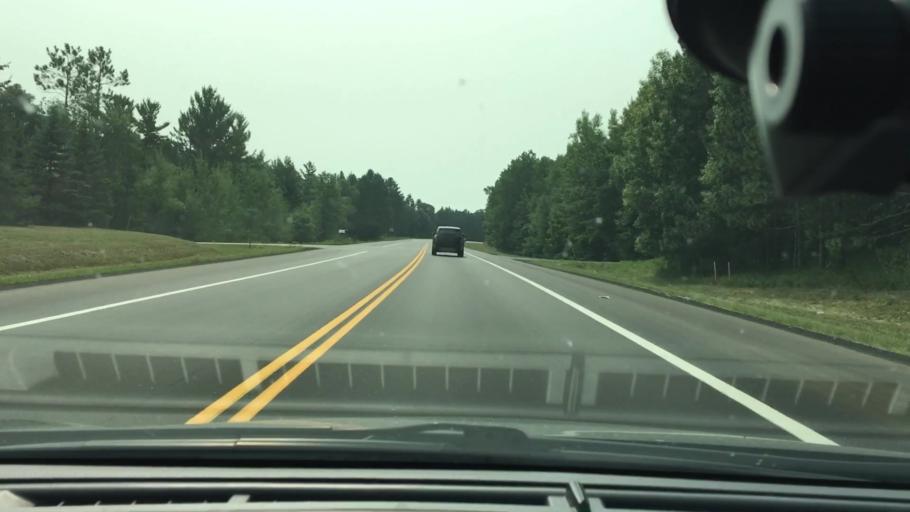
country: US
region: Minnesota
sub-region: Crow Wing County
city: Brainerd
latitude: 46.4157
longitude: -94.1780
